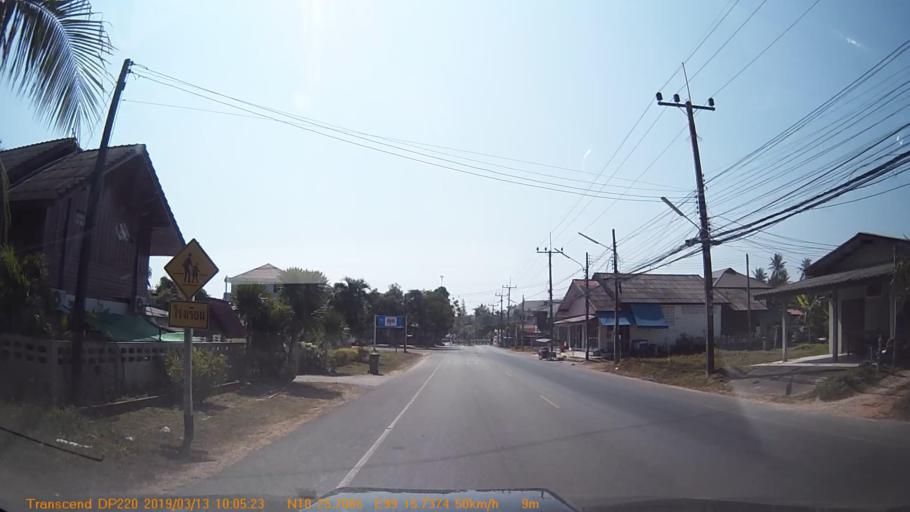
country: TH
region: Chumphon
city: Chumphon
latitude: 10.4283
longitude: 99.2624
